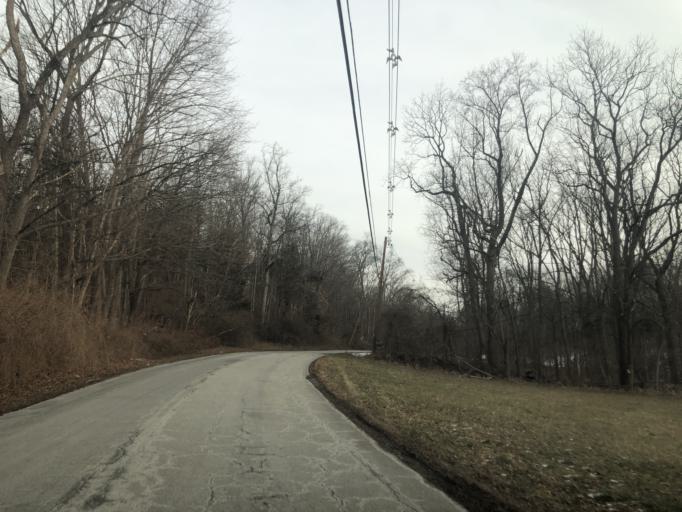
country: US
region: New Jersey
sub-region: Warren County
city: Oxford
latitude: 40.9153
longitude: -74.9724
